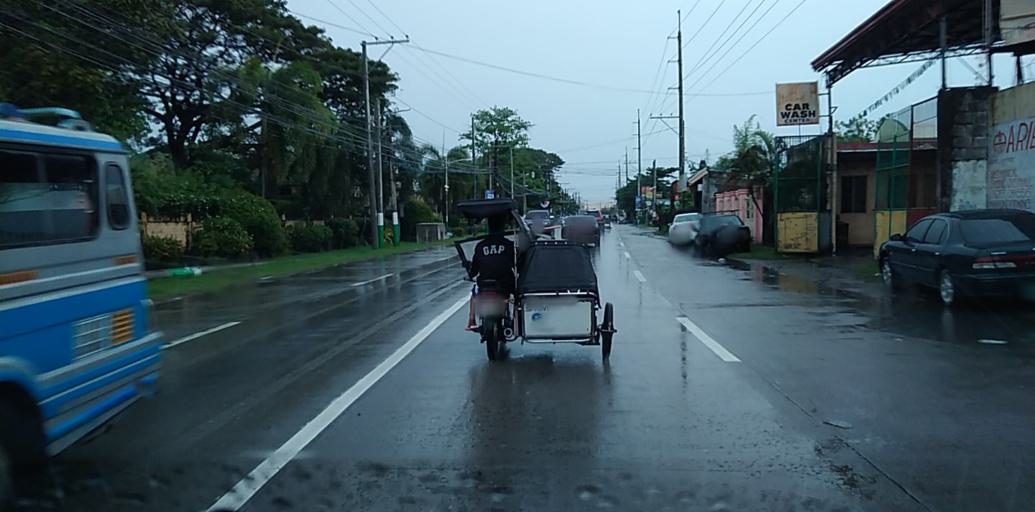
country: PH
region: Central Luzon
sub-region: Province of Pampanga
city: Mexico
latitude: 15.0552
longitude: 120.7132
